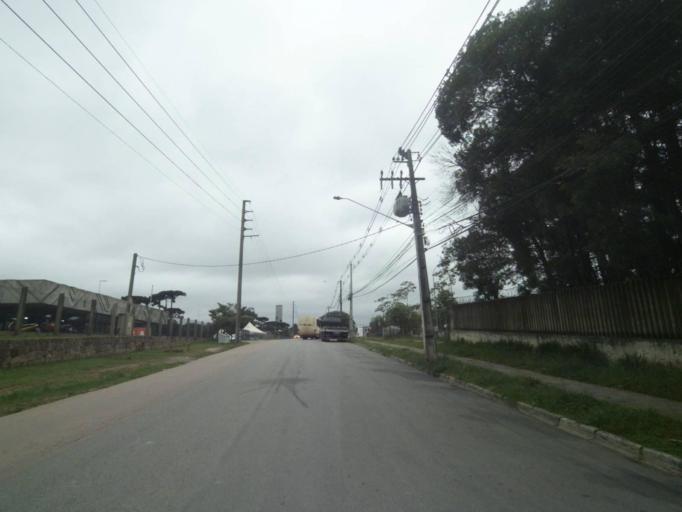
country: BR
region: Parana
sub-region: Araucaria
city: Araucaria
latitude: -25.5591
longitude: -49.3105
